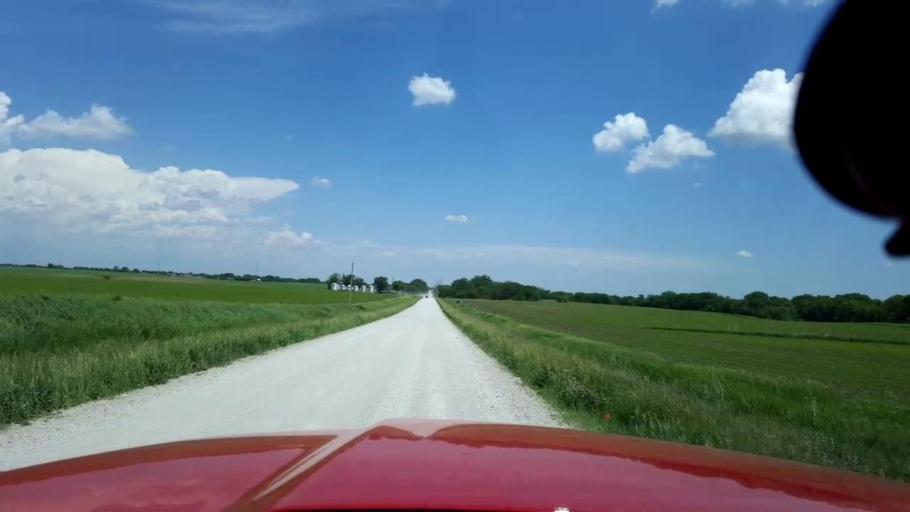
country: US
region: Iowa
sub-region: Boone County
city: Boone
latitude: 42.0493
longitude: -93.7684
